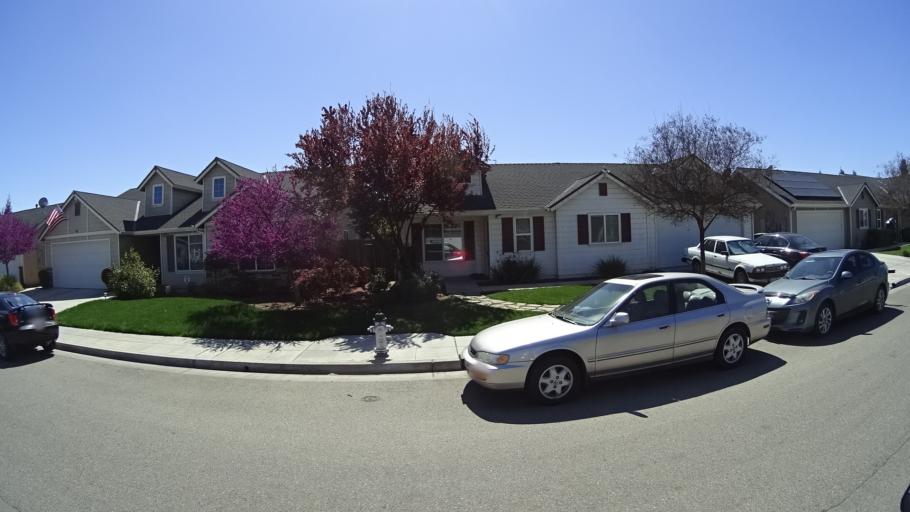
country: US
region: California
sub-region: Fresno County
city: West Park
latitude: 36.7762
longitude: -119.8835
